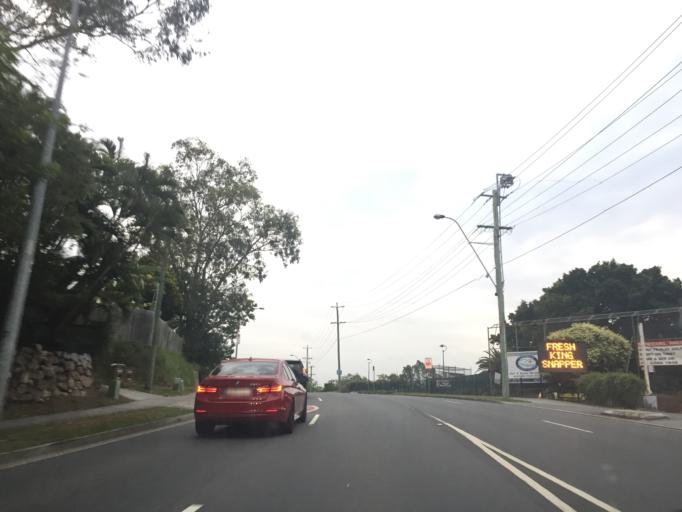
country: AU
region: Queensland
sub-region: Brisbane
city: Toowong
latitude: -27.4464
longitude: 152.9618
